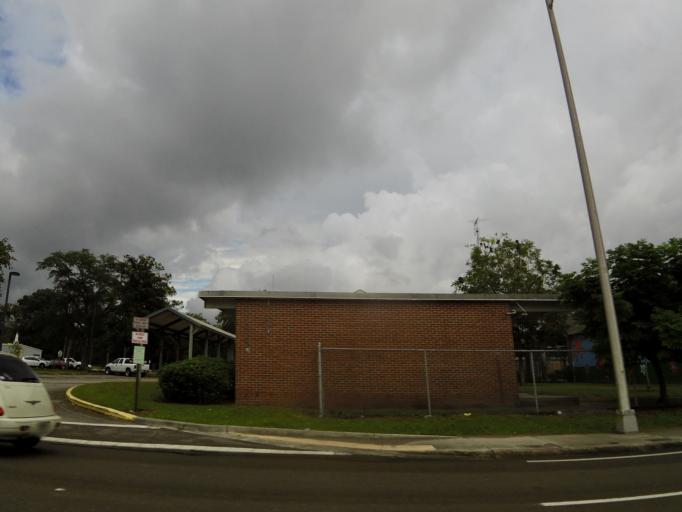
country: US
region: Florida
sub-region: Duval County
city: Baldwin
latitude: 30.3122
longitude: -81.8486
